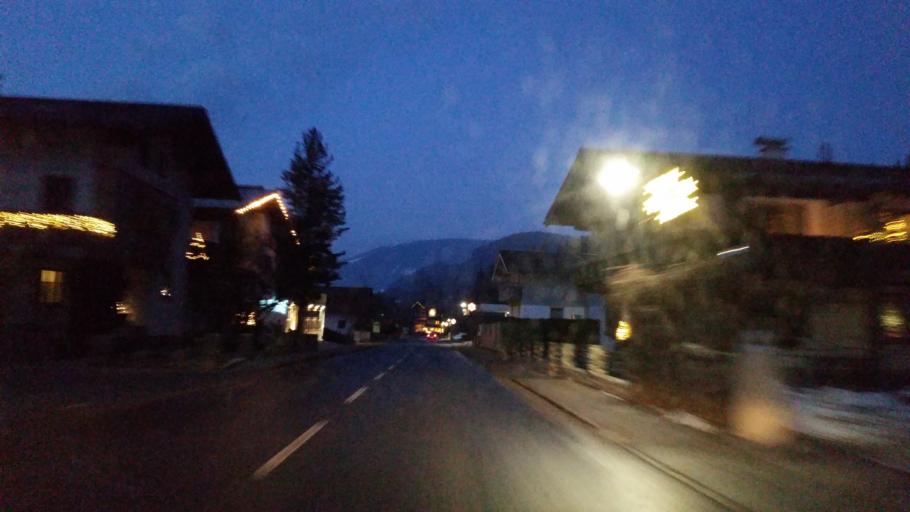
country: AT
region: Salzburg
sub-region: Politischer Bezirk Hallein
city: Abtenau
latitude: 47.5158
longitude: 13.4313
